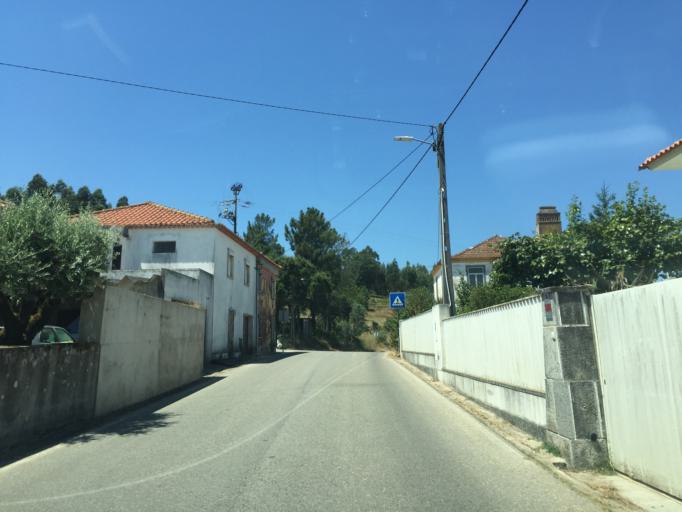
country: PT
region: Santarem
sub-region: Ferreira do Zezere
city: Ferreira do Zezere
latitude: 39.5973
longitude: -8.2962
